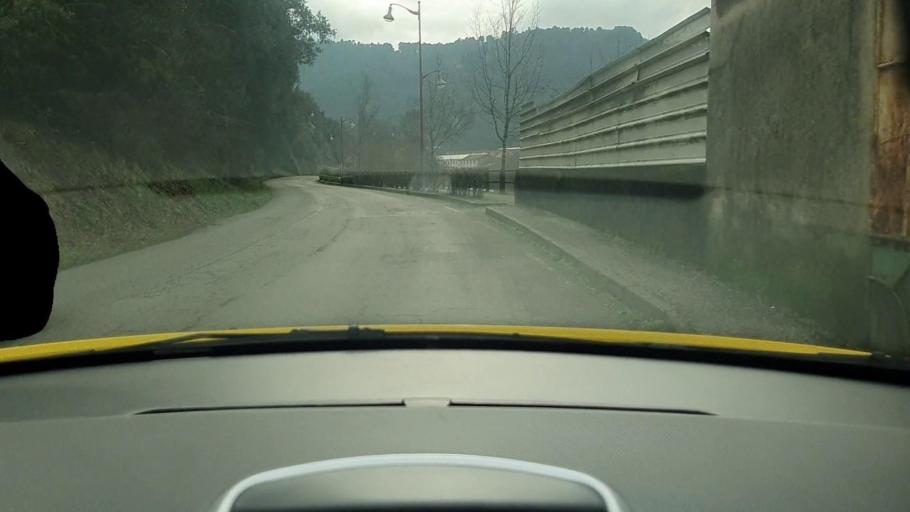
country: FR
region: Languedoc-Roussillon
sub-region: Departement du Gard
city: Besseges
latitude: 44.2974
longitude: 4.0938
